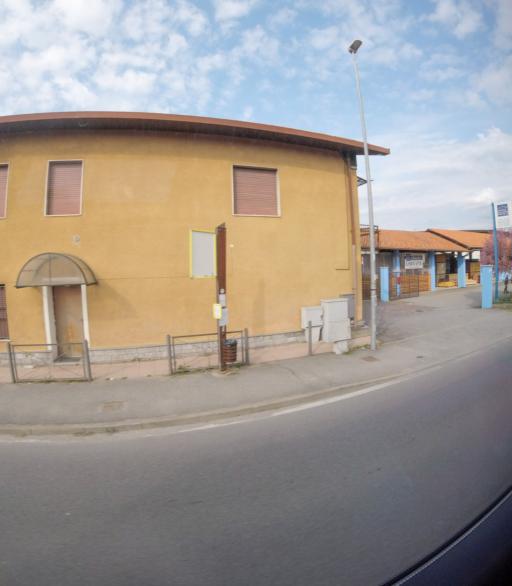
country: IT
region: Piedmont
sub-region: Provincia di Novara
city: Gozzano
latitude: 45.7316
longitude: 8.4429
